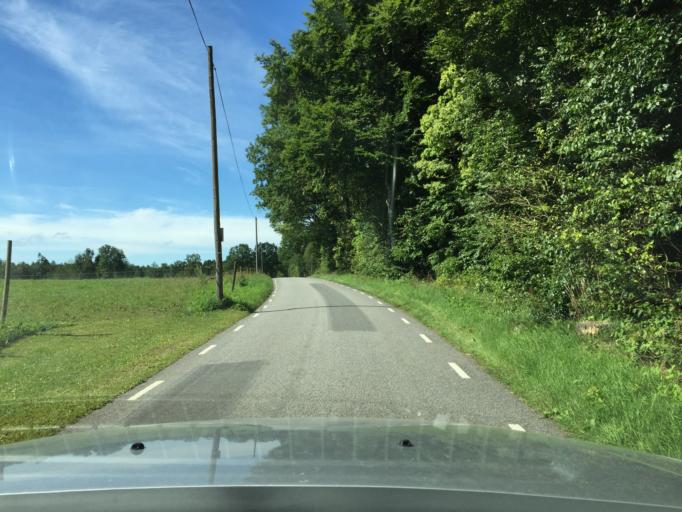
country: SE
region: Skane
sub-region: Hassleholms Kommun
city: Sosdala
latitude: 56.0333
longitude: 13.6467
